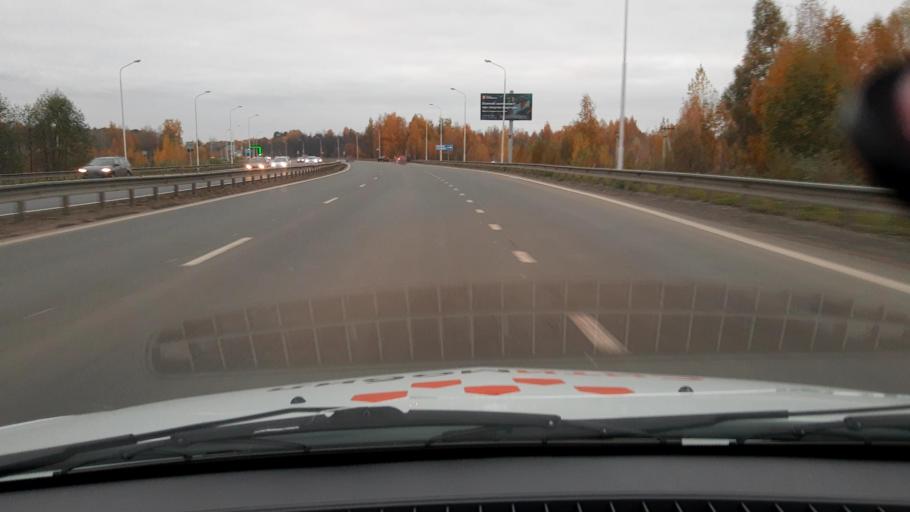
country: RU
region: Bashkortostan
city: Ufa
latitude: 54.6633
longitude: 56.0774
